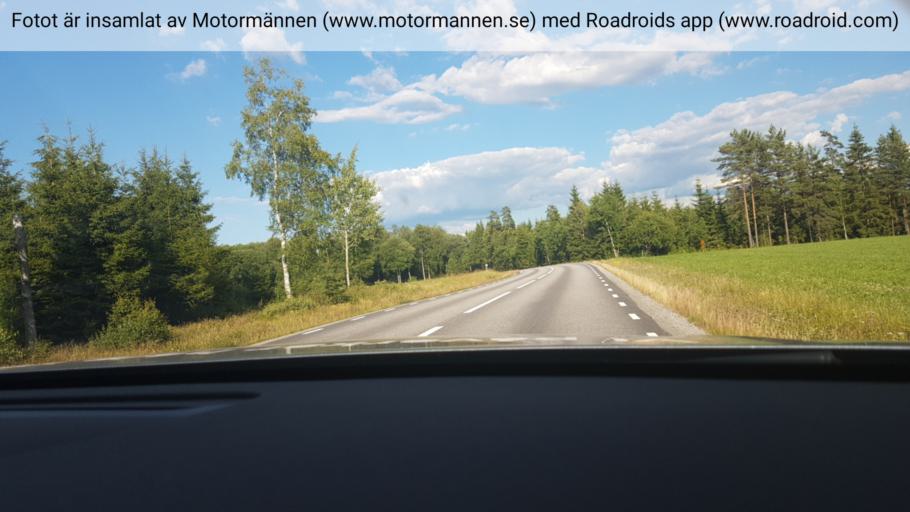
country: SE
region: Vaestra Goetaland
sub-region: Tranemo Kommun
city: Limmared
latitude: 57.5708
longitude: 13.5398
